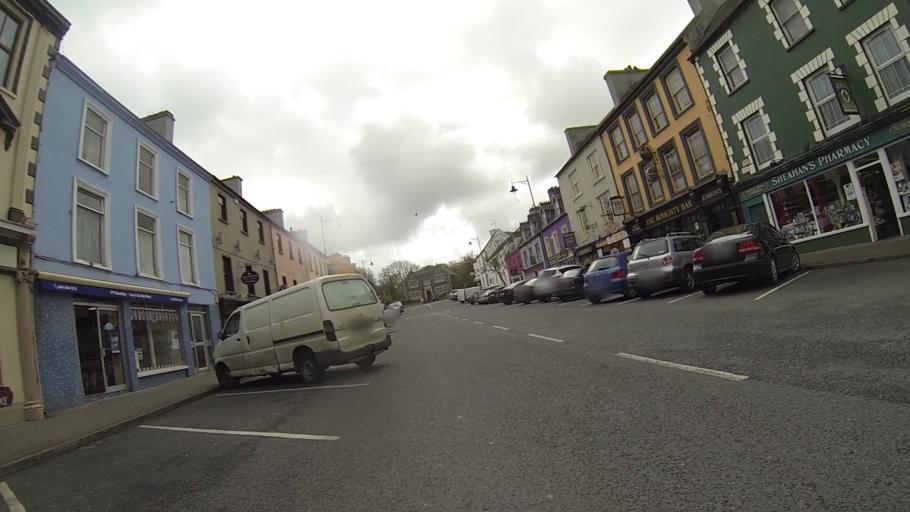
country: IE
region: Munster
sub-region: Ciarrai
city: Kenmare
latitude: 51.8797
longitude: -9.5826
